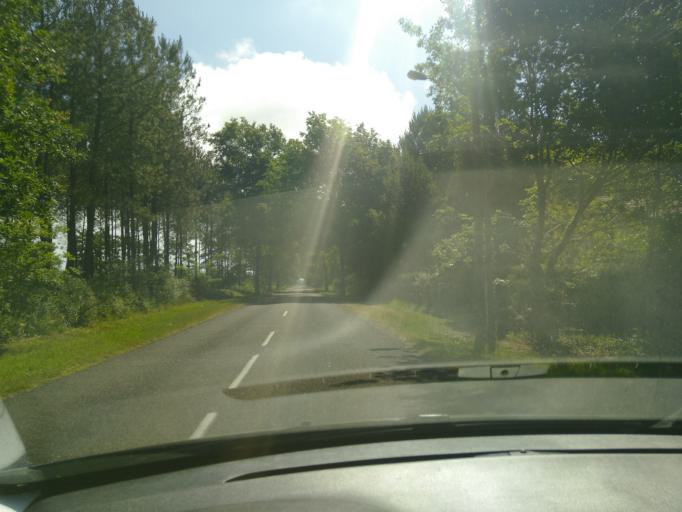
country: FR
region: Aquitaine
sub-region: Departement des Landes
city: Saint-Vincent-de-Paul
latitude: 43.7842
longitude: -0.9835
